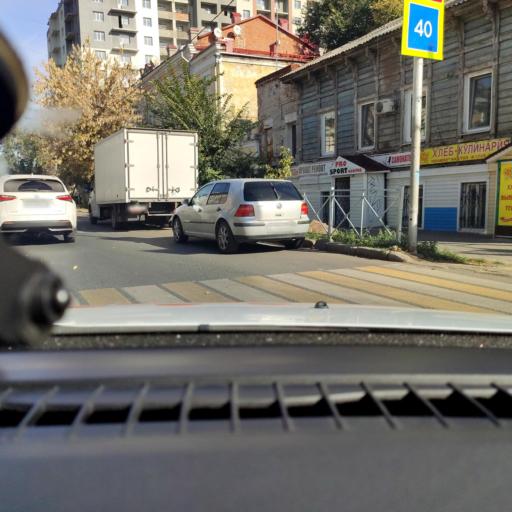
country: RU
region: Samara
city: Rozhdestveno
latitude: 53.1810
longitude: 50.0846
